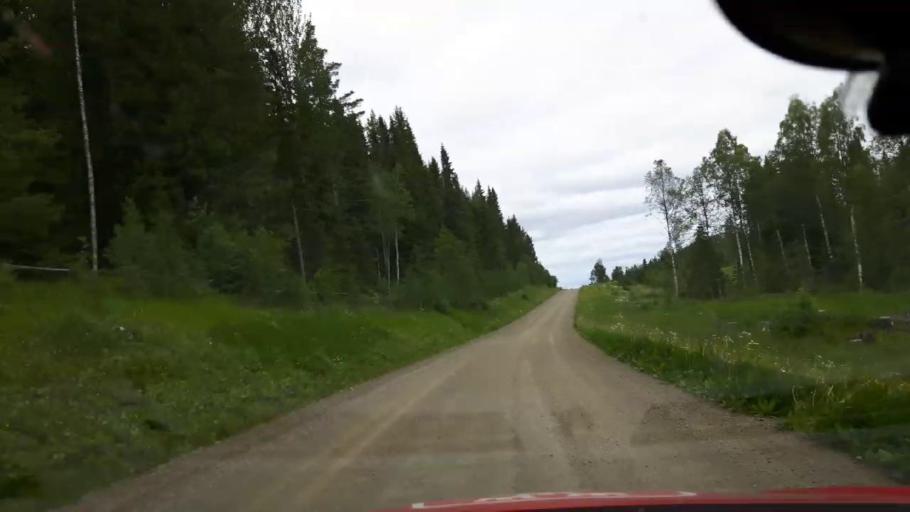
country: SE
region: Jaemtland
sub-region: OEstersunds Kommun
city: Brunflo
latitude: 62.9281
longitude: 15.0014
